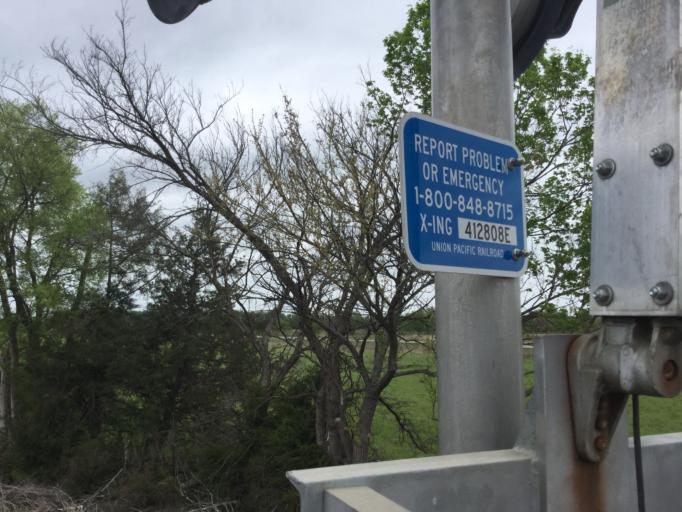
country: US
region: Kansas
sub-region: Labette County
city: Parsons
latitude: 37.3110
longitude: -95.2505
